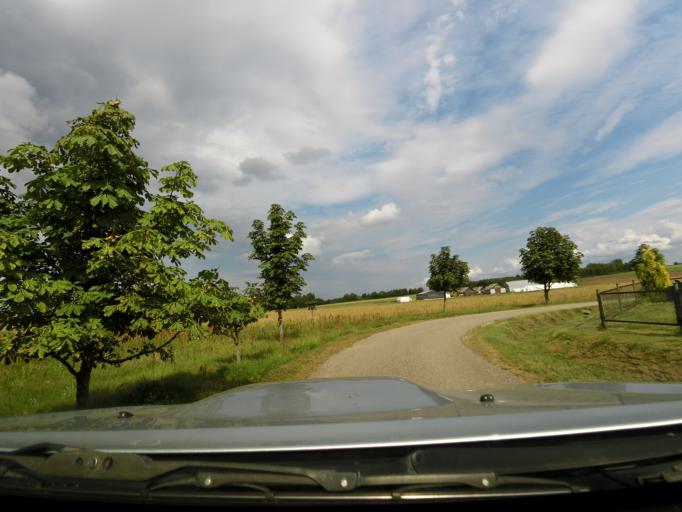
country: LT
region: Vilnius County
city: Elektrenai
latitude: 54.9124
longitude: 24.7232
